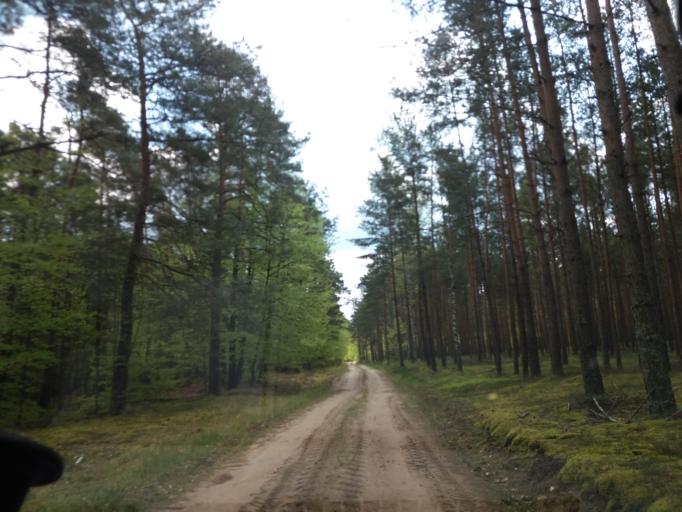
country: PL
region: West Pomeranian Voivodeship
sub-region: Powiat choszczenski
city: Drawno
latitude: 53.1533
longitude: 15.8065
